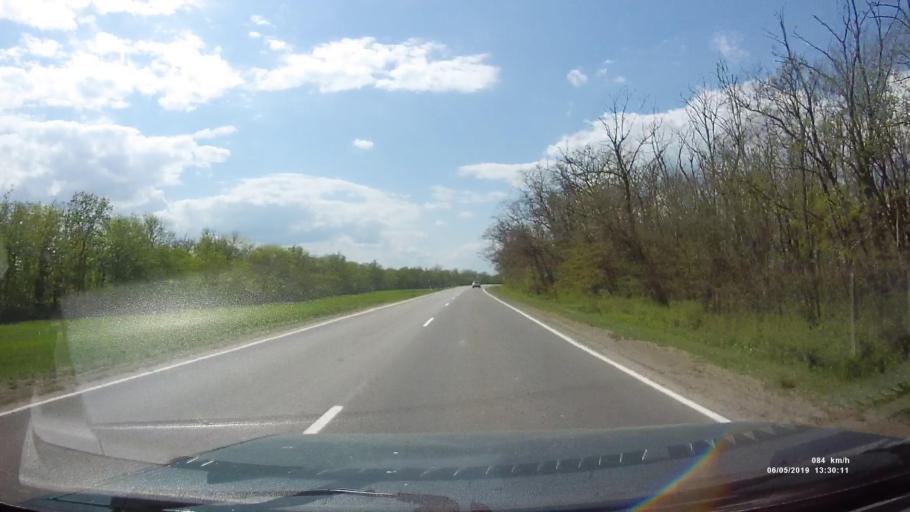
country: RU
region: Rostov
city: Ust'-Donetskiy
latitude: 47.6709
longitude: 40.8311
